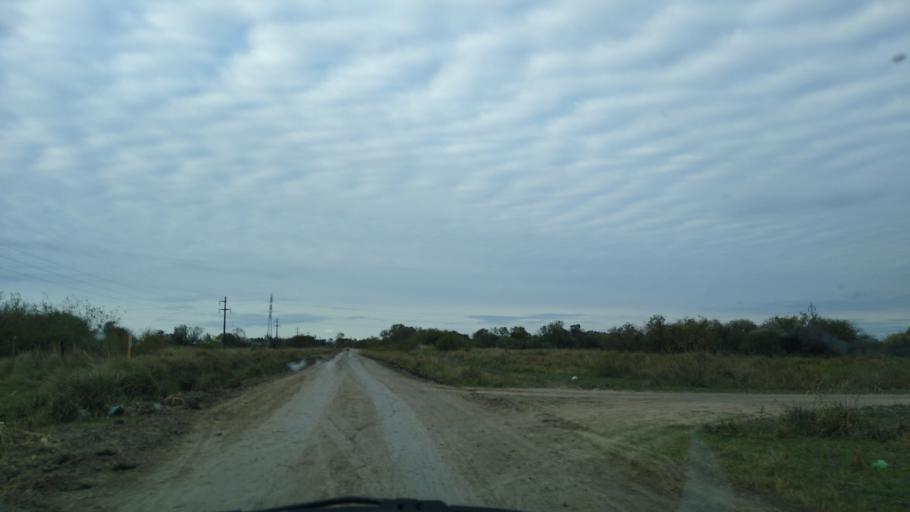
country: AR
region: Chaco
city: Fontana
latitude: -27.3886
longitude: -59.0476
